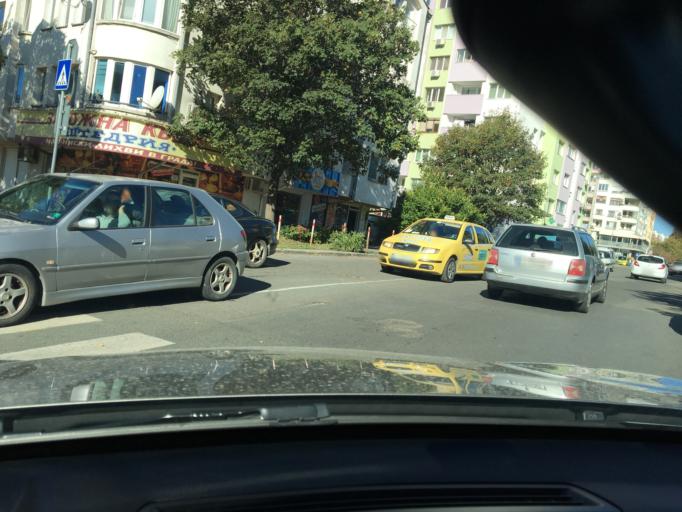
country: BG
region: Burgas
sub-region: Obshtina Burgas
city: Burgas
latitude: 42.5202
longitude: 27.4518
